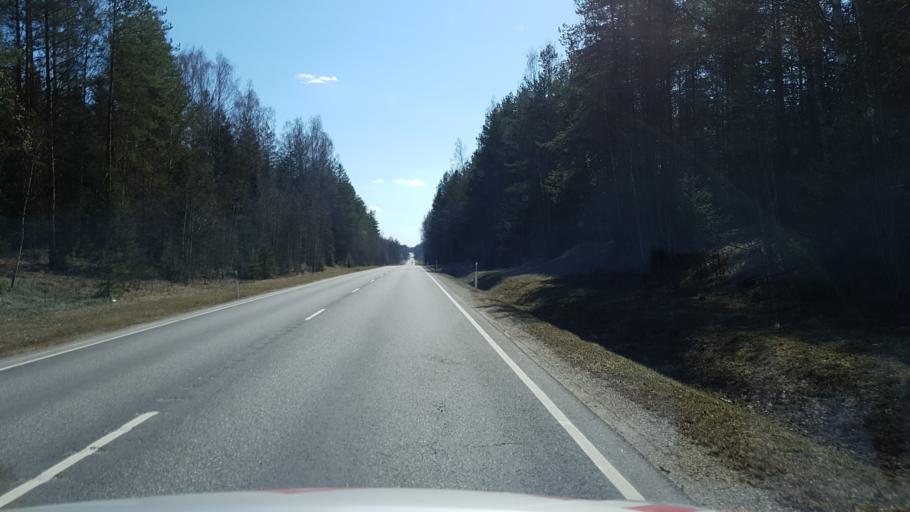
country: EE
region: Jogevamaa
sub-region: Mustvee linn
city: Mustvee
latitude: 58.6905
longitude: 26.8101
